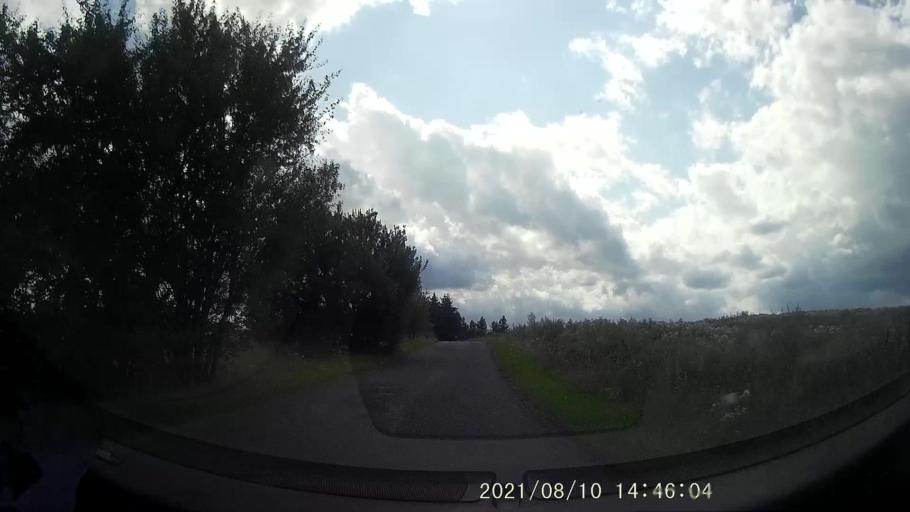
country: PL
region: Lower Silesian Voivodeship
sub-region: Powiat klodzki
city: Radkow
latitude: 50.5308
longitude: 16.4138
